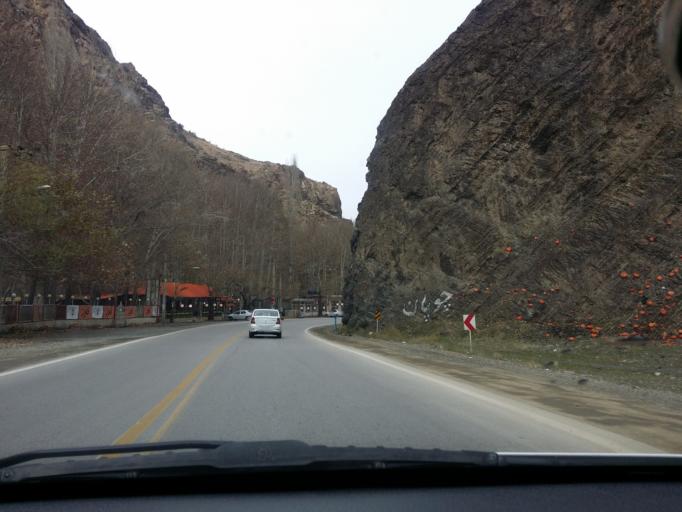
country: IR
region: Tehran
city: Tajrish
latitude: 36.0192
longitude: 51.2687
